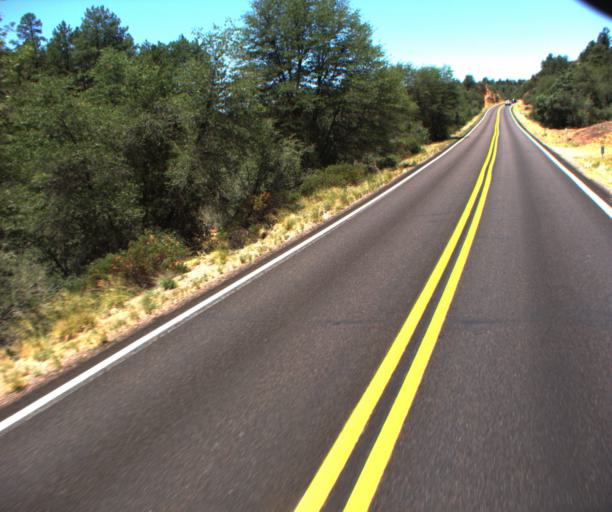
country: US
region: Arizona
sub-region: Gila County
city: Payson
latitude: 34.2852
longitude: -111.3357
